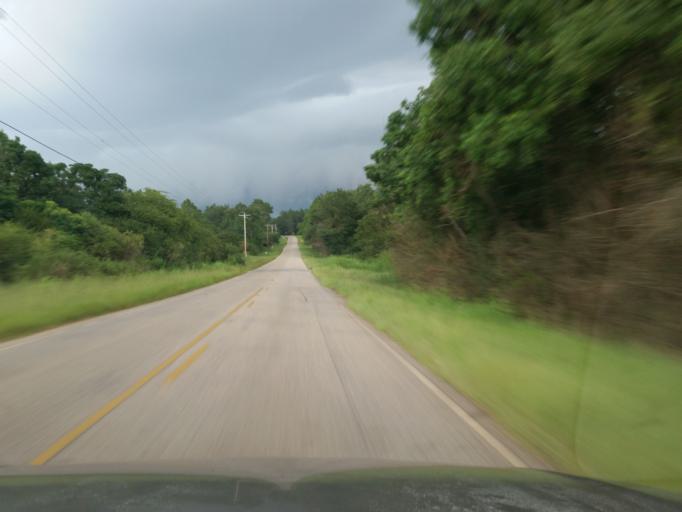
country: US
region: Alabama
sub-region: Baldwin County
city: Robertsdale
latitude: 30.5756
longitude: -87.5762
